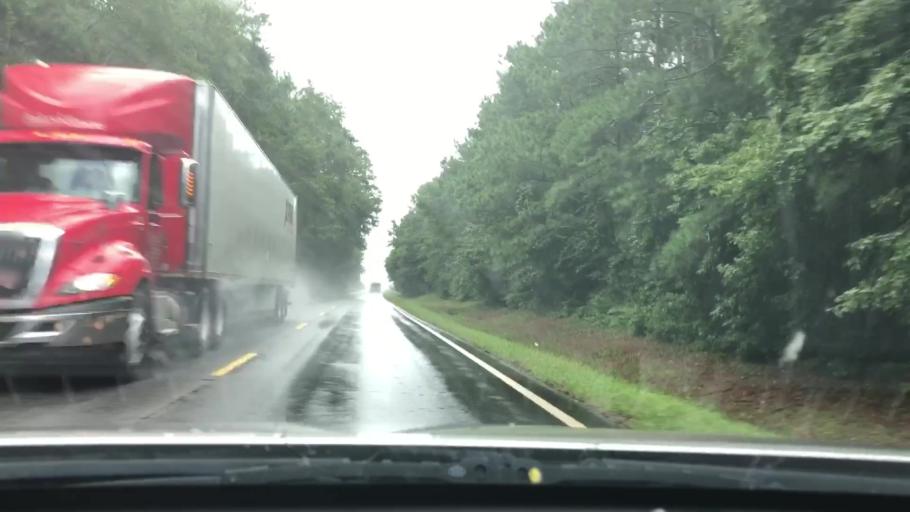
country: US
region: Georgia
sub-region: Lamar County
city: Barnesville
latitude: 33.0624
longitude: -84.2130
